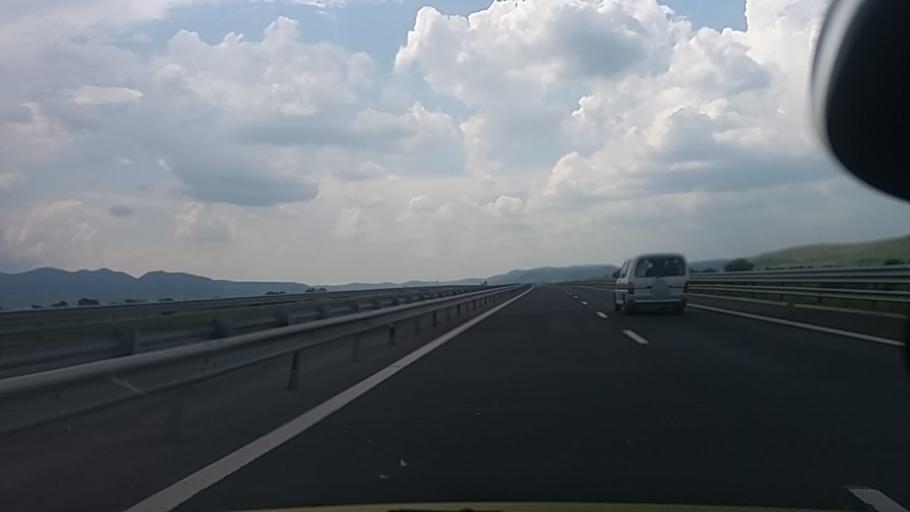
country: RO
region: Hunedoara
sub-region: Oras Simeria
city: Simeria
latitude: 45.8822
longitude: 22.9908
